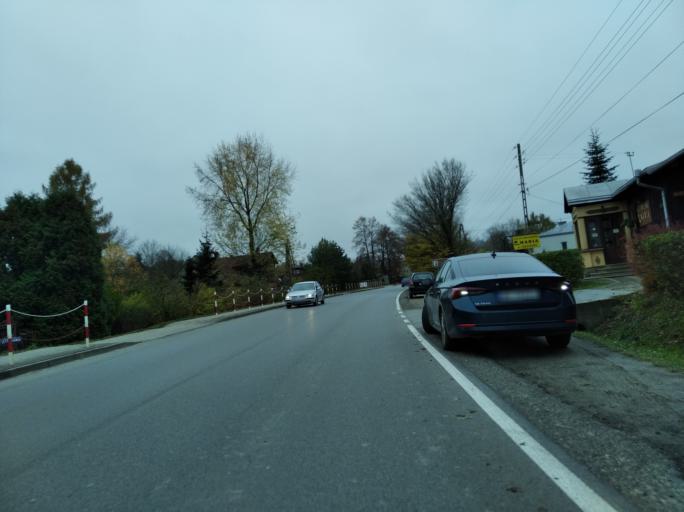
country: PL
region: Subcarpathian Voivodeship
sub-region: Powiat krosnienski
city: Chorkowka
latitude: 49.6698
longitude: 21.6933
